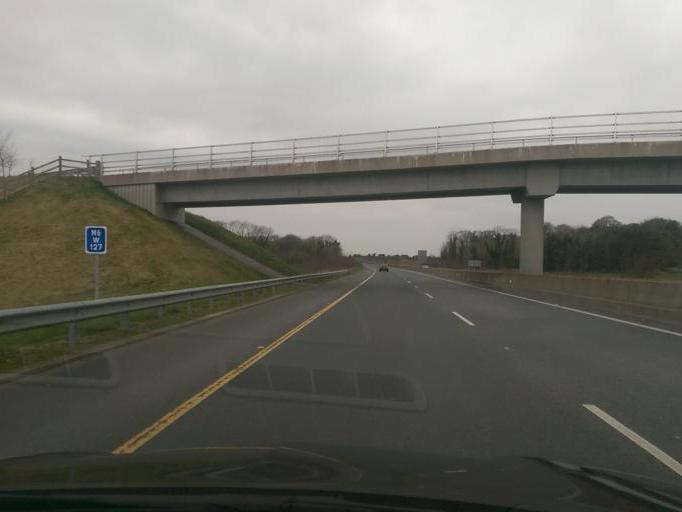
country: IE
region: Connaught
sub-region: County Galway
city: Athenry
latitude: 53.2932
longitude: -8.7763
